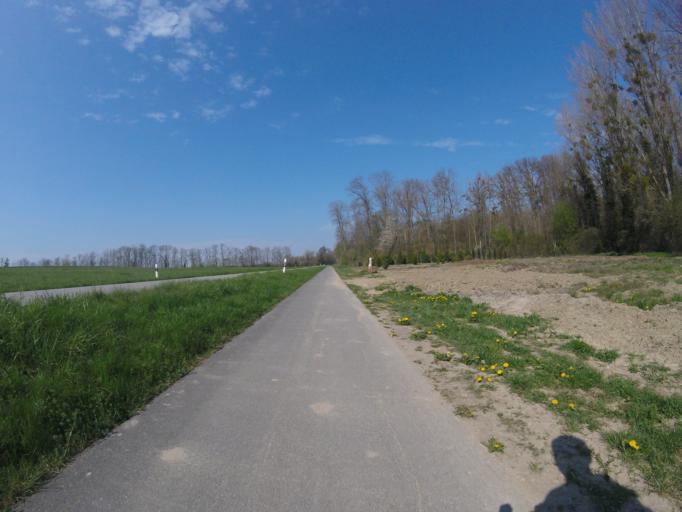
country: CH
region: Vaud
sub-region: Broye-Vully District
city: Avenches
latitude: 46.9020
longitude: 7.0604
